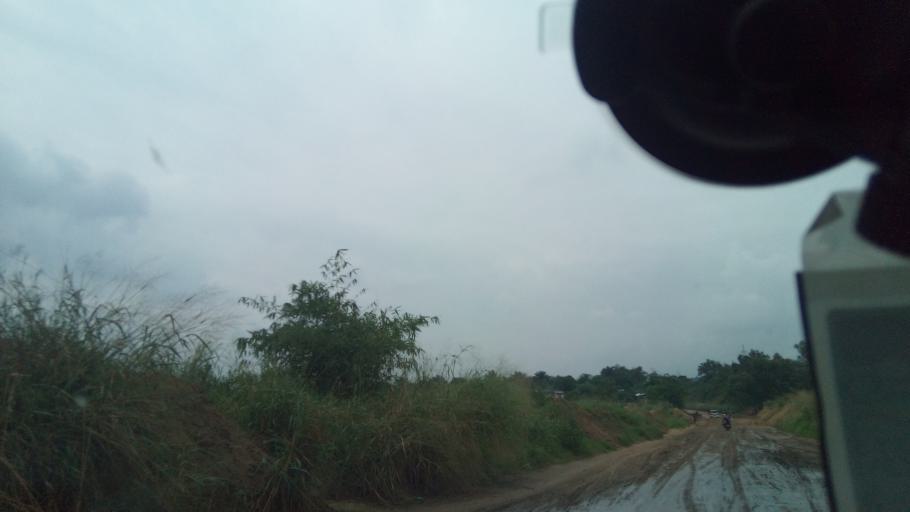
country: CG
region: Brazzaville
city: Brazzaville
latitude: -4.0769
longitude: 15.5437
